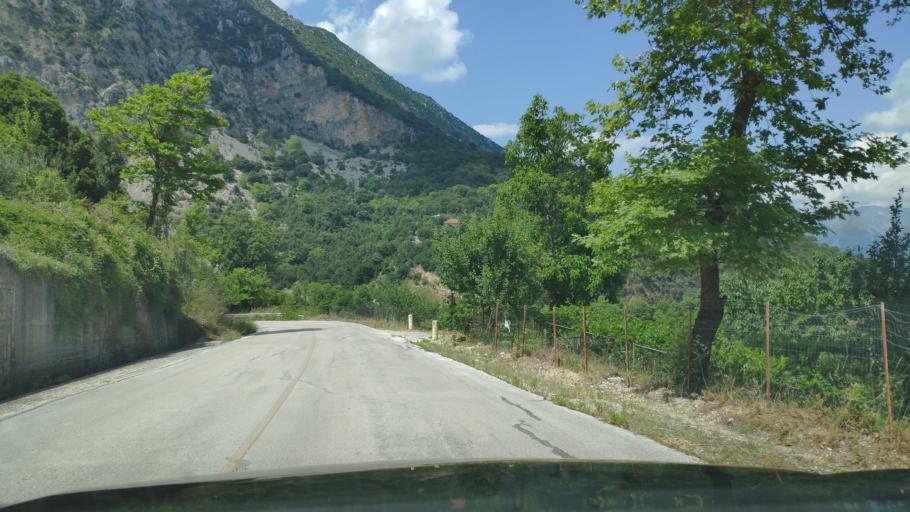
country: GR
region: Epirus
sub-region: Nomos Artas
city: Agios Dimitrios
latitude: 39.3431
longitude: 21.0070
